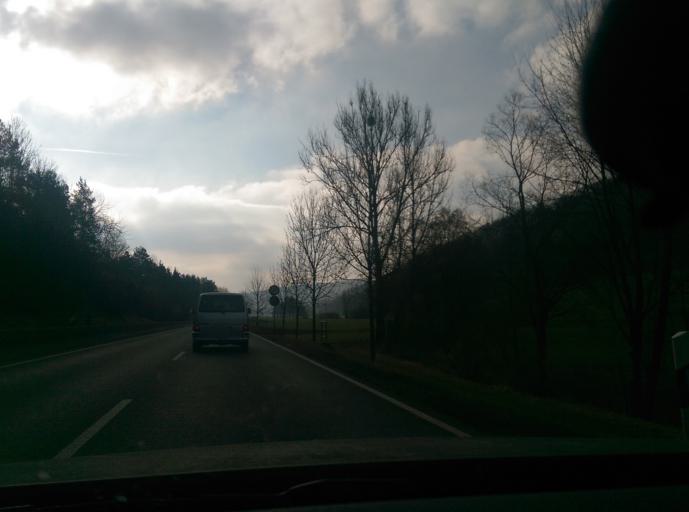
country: DE
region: Hesse
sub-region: Regierungsbezirk Kassel
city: Sontra
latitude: 51.0594
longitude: 10.0012
